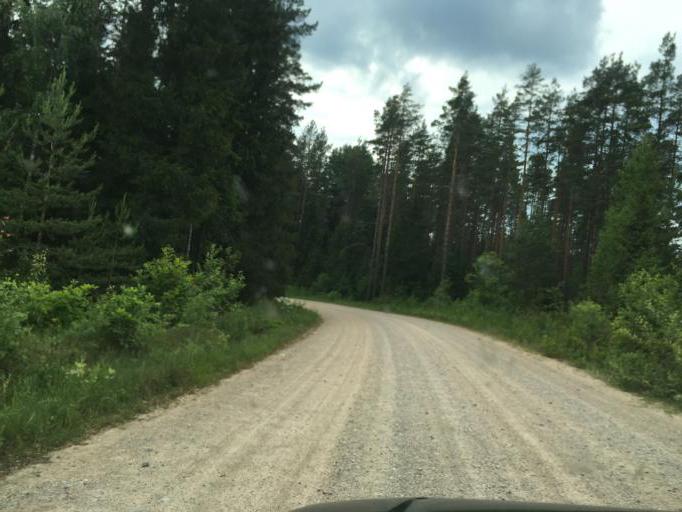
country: LV
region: Vilanu
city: Vilani
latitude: 56.7455
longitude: 27.0587
